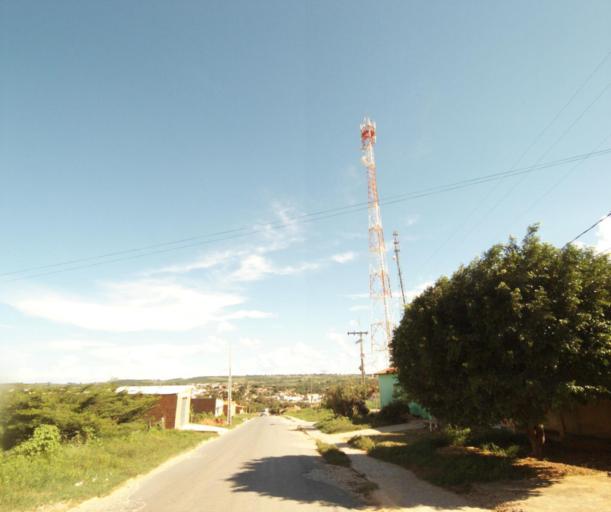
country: BR
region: Bahia
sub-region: Correntina
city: Correntina
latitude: -13.3358
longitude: -44.6379
